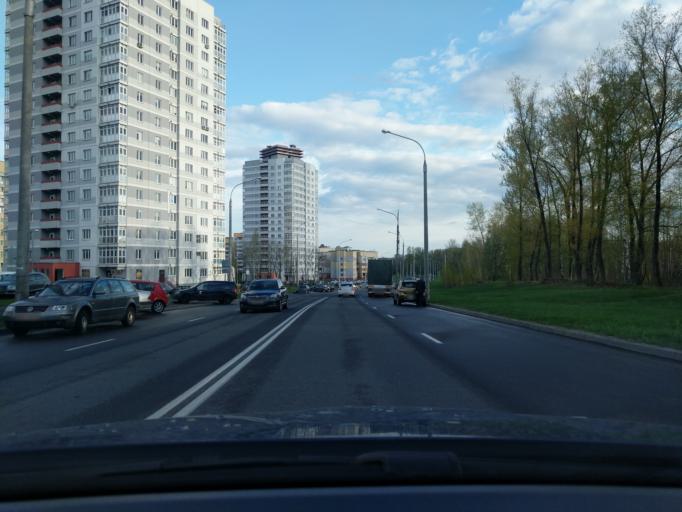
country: BY
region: Minsk
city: Novoye Medvezhino
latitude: 53.8974
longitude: 27.4746
